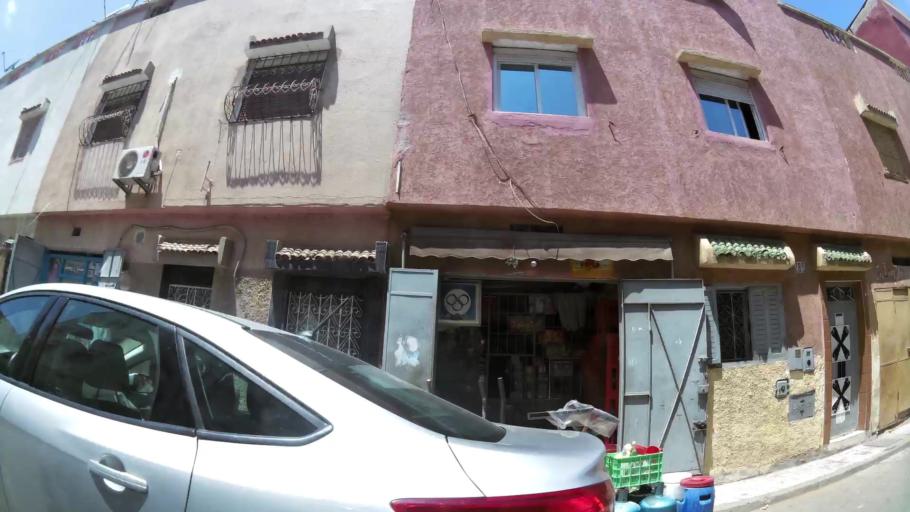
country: MA
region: Gharb-Chrarda-Beni Hssen
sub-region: Kenitra Province
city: Kenitra
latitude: 34.2643
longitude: -6.5559
